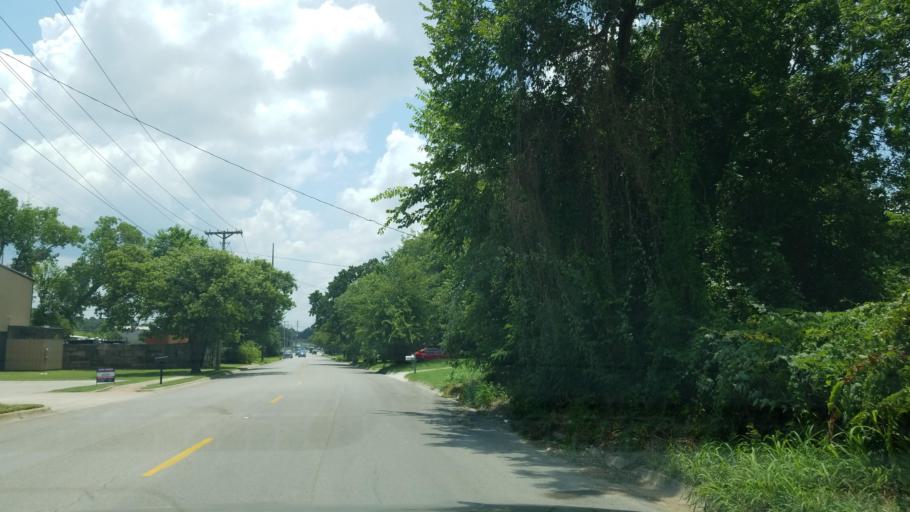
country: US
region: Texas
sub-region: Denton County
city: Denton
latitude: 33.2037
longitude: -97.1230
